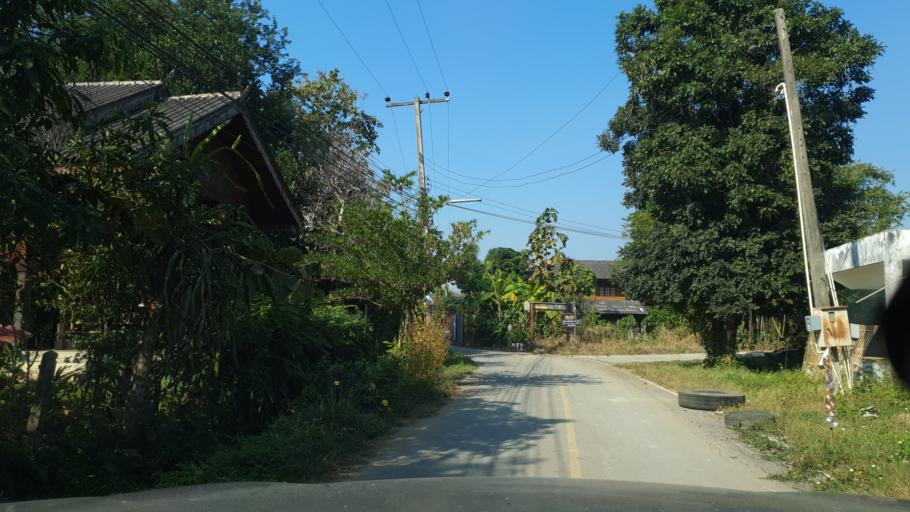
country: TH
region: Lamphun
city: Ban Thi
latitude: 18.6856
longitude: 99.0998
